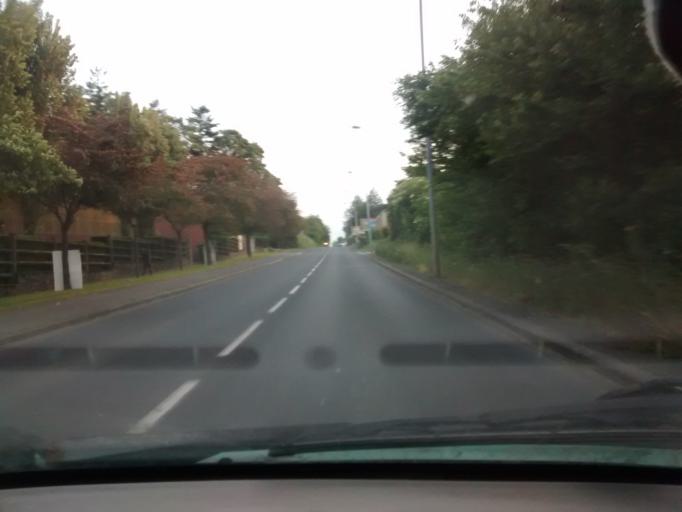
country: FR
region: Lower Normandy
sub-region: Departement de la Manche
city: Agneaux
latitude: 49.1056
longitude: -1.1103
